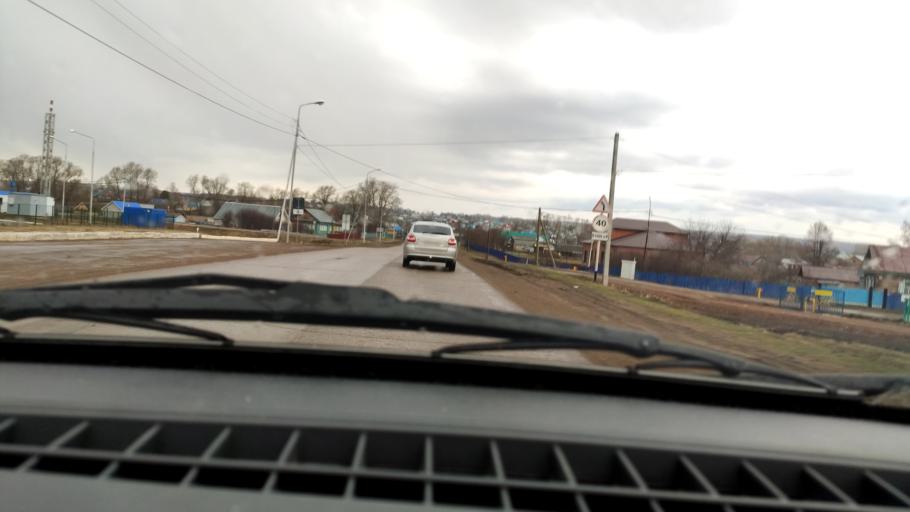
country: RU
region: Bashkortostan
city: Chekmagush
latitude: 55.1326
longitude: 54.6758
